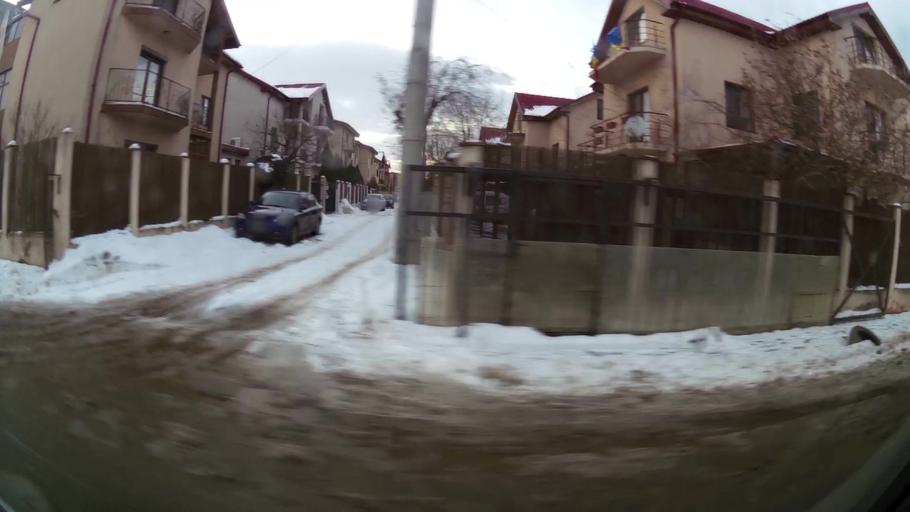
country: RO
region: Ilfov
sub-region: Comuna Popesti-Leordeni
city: Popesti-Leordeni
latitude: 44.3693
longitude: 26.1556
